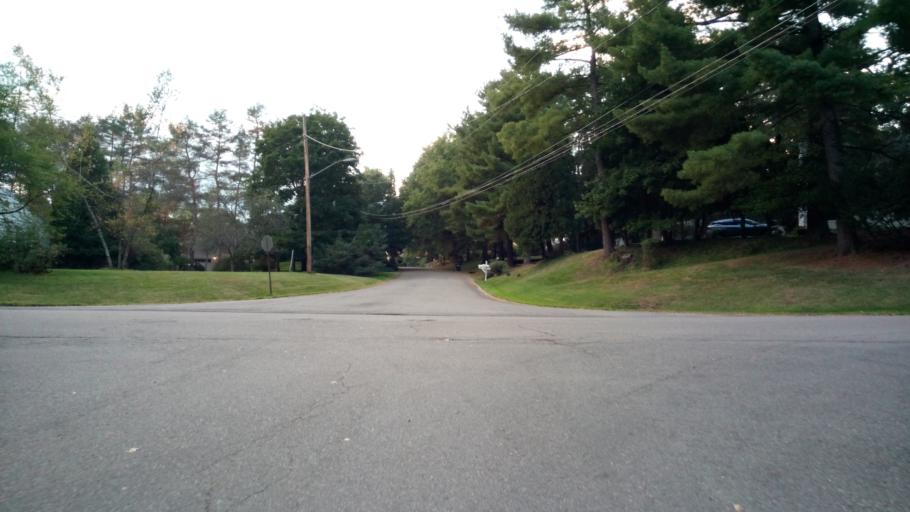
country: US
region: New York
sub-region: Chemung County
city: West Elmira
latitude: 42.0895
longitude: -76.8355
